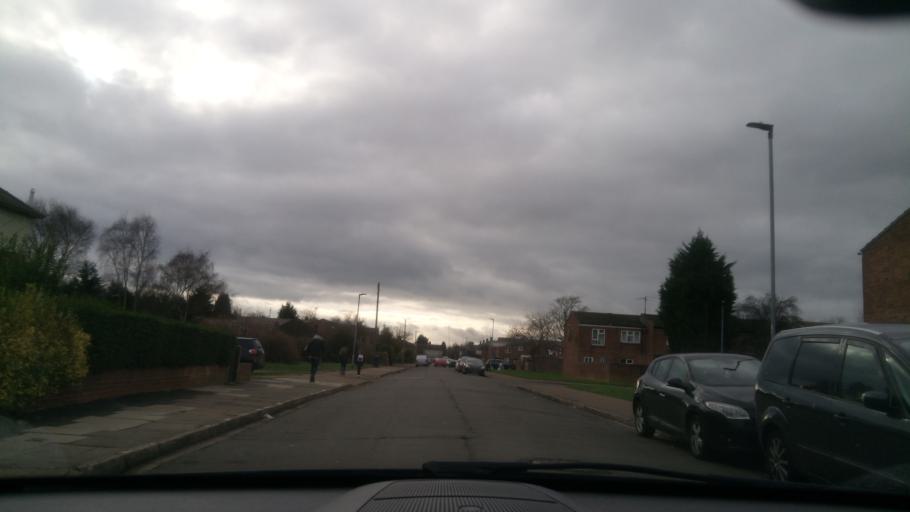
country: GB
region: England
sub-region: Peterborough
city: Peterborough
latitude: 52.5810
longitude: -0.2246
